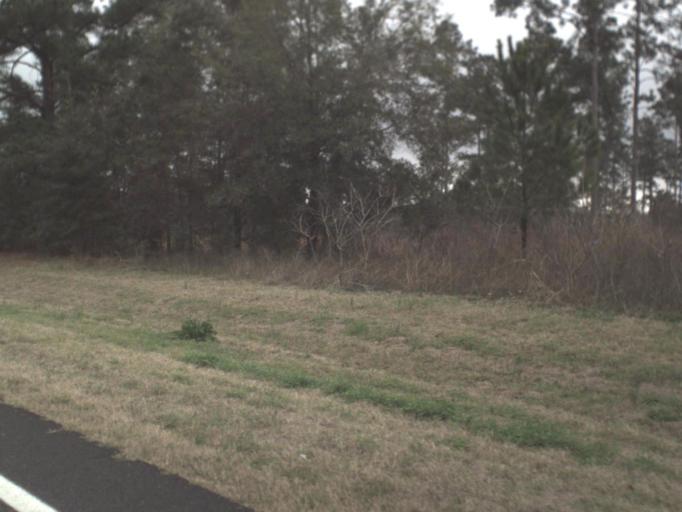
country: US
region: Florida
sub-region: Jefferson County
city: Monticello
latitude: 30.4114
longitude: -83.9337
